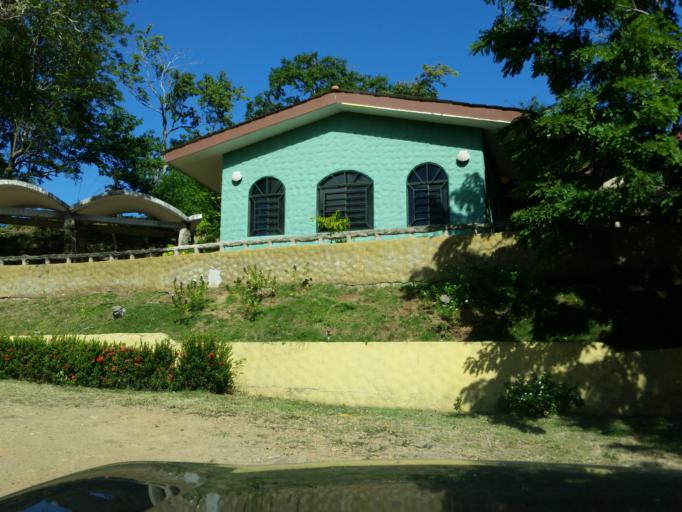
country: NI
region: Rivas
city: San Juan del Sur
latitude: 11.2729
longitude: -85.8404
